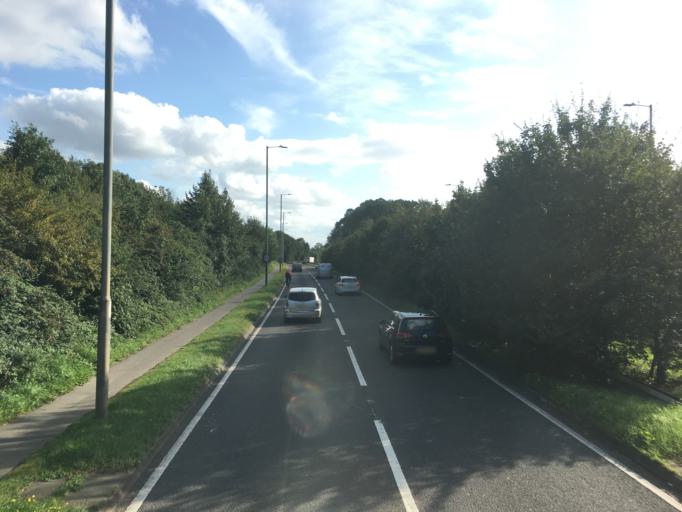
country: GB
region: England
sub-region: Warwickshire
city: Rugby
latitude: 52.3989
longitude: -1.2477
